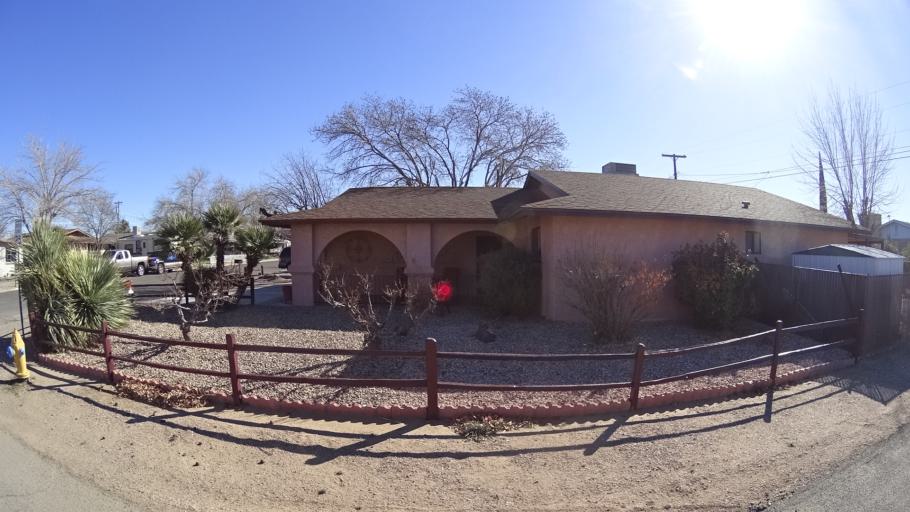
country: US
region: Arizona
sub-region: Mohave County
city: Kingman
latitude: 35.2073
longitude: -114.0269
